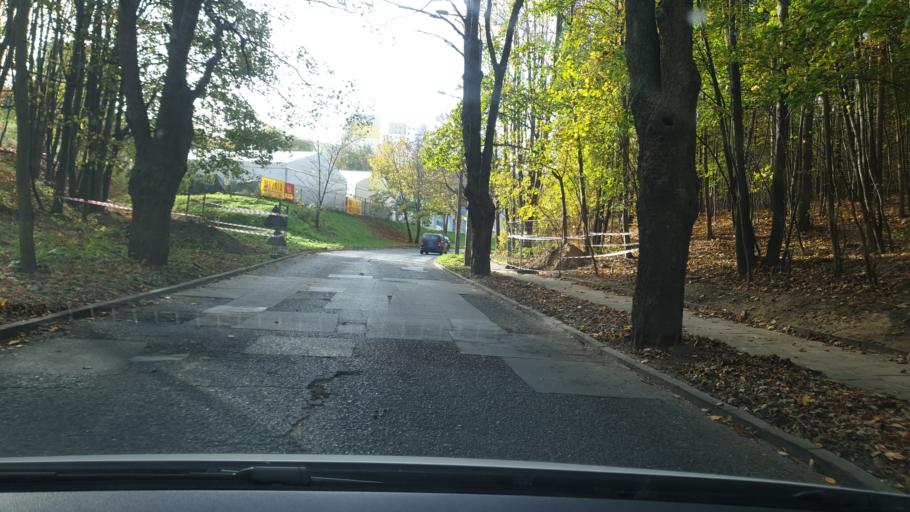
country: PL
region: Pomeranian Voivodeship
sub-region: Powiat gdanski
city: Kowale
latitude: 54.3622
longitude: 18.5861
